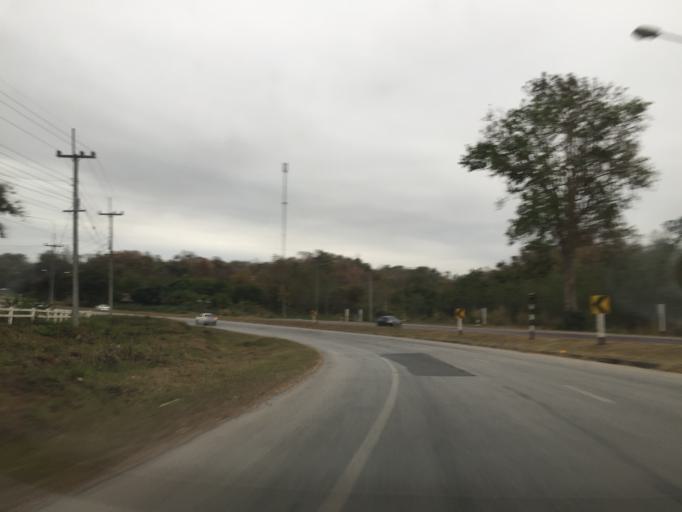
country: TH
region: Loei
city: Erawan
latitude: 17.3080
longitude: 101.9376
